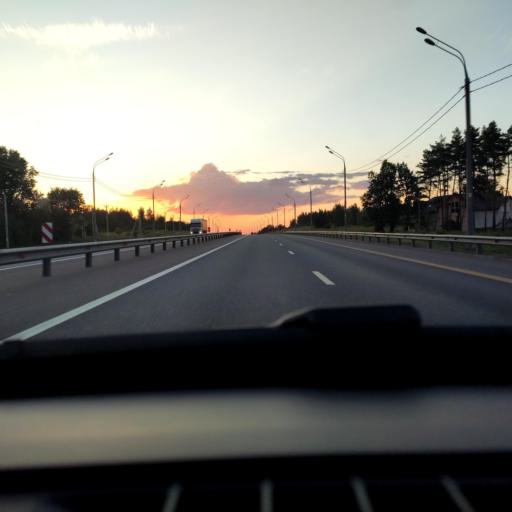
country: RU
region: Lipetsk
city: Zadonsk
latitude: 52.3565
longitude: 38.9424
